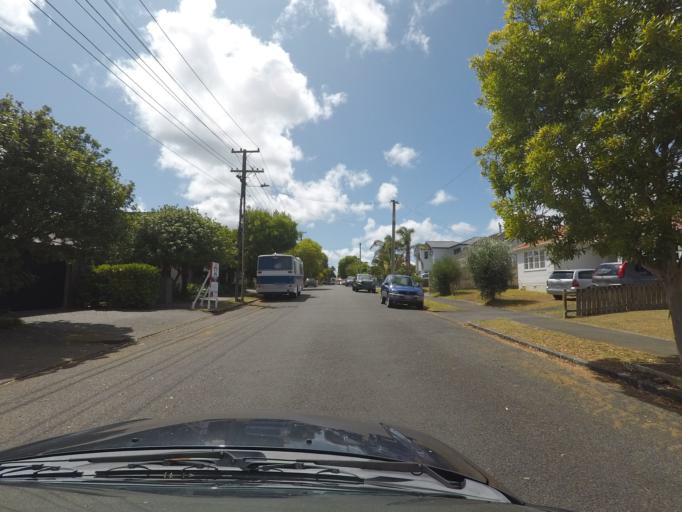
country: NZ
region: Auckland
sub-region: Auckland
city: Rosebank
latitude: -36.8630
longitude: 174.7020
